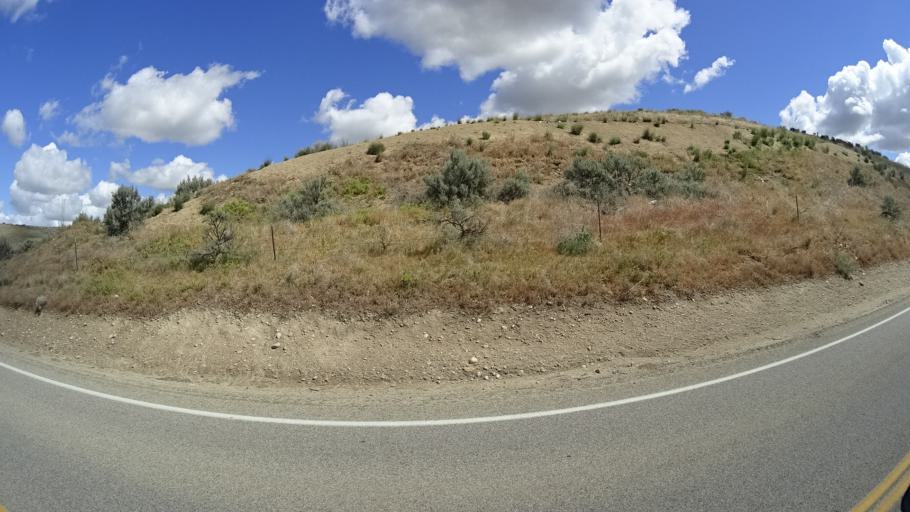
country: US
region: Idaho
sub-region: Ada County
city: Kuna
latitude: 43.5040
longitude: -116.3004
